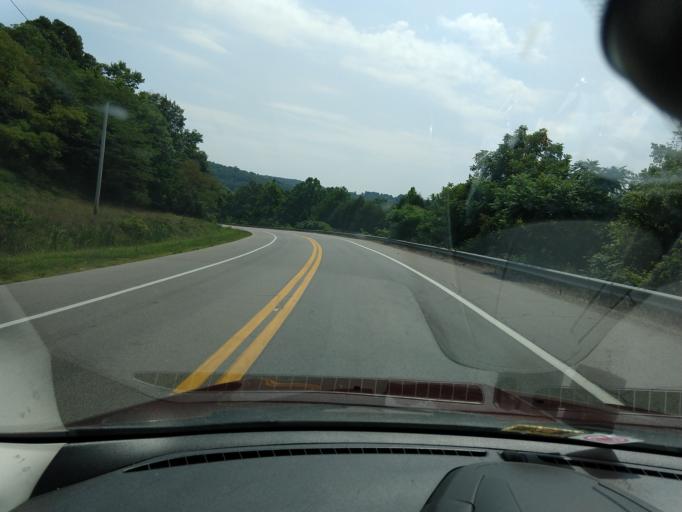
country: US
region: West Virginia
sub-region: Jackson County
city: Ravenswood
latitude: 38.8595
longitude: -81.8168
